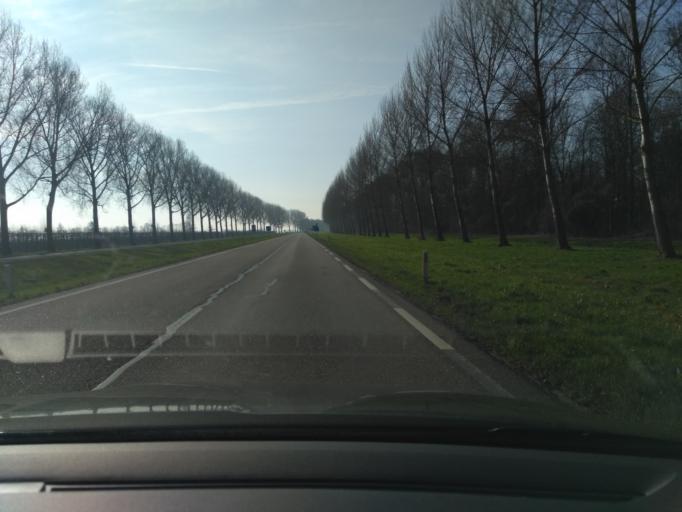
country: NL
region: Flevoland
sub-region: Gemeente Dronten
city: Dronten
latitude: 52.5211
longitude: 5.7342
